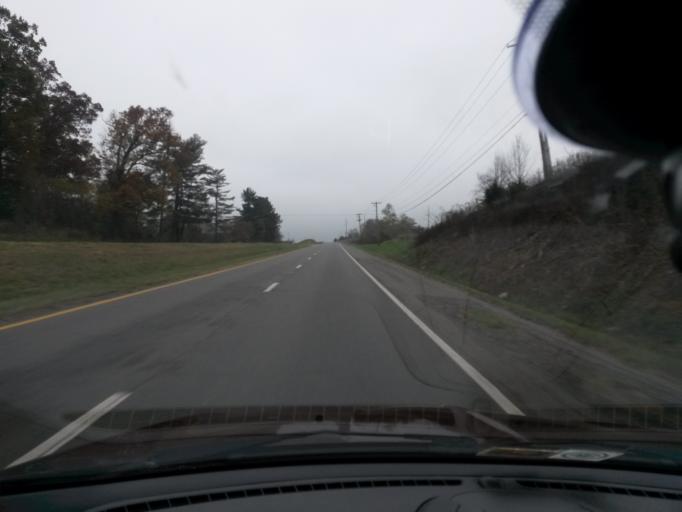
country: US
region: Virginia
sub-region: Botetourt County
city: Daleville
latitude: 37.4360
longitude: -79.9036
